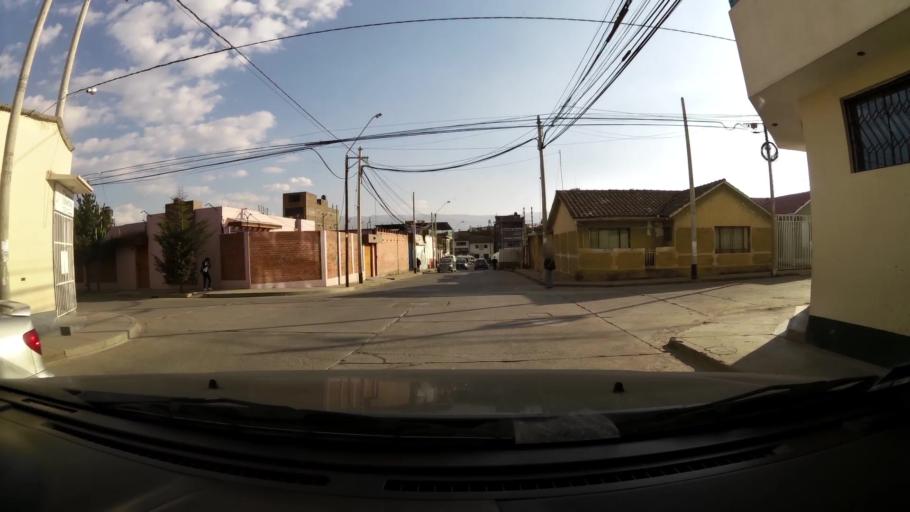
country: PE
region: Junin
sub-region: Provincia de Huancayo
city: El Tambo
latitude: -12.0508
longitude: -75.2202
